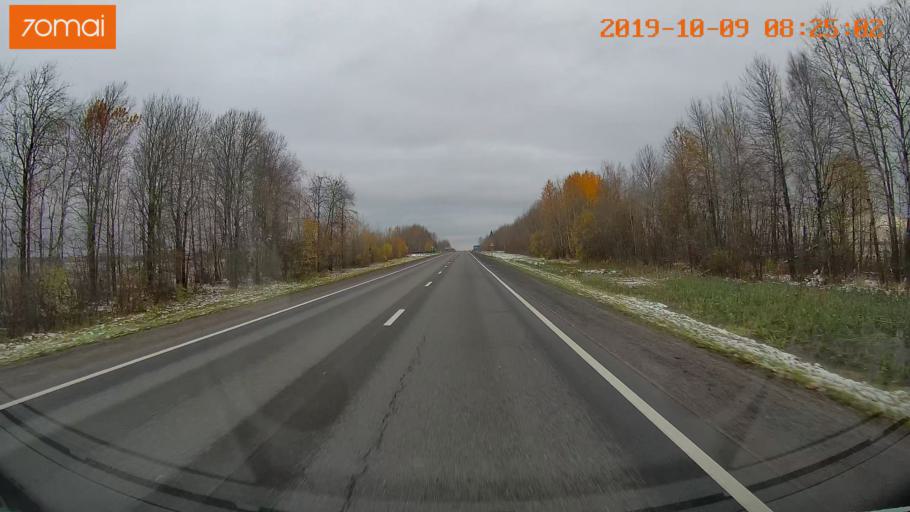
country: RU
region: Vologda
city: Gryazovets
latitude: 58.7749
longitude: 40.2748
